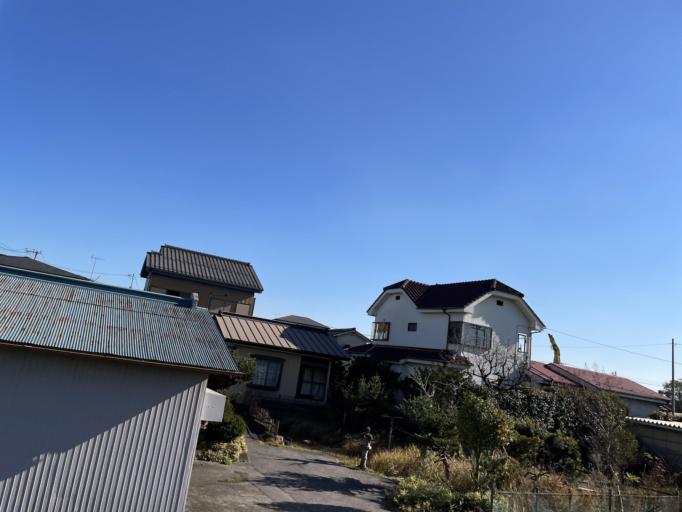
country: JP
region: Saitama
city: Yashio-shi
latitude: 35.8405
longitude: 139.8405
